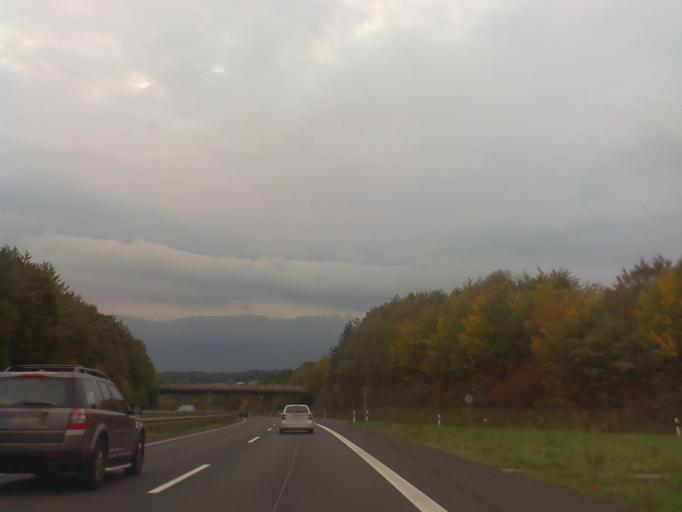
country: DE
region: Hesse
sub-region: Regierungsbezirk Darmstadt
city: Steinau an der Strasse
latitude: 50.3197
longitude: 9.4368
